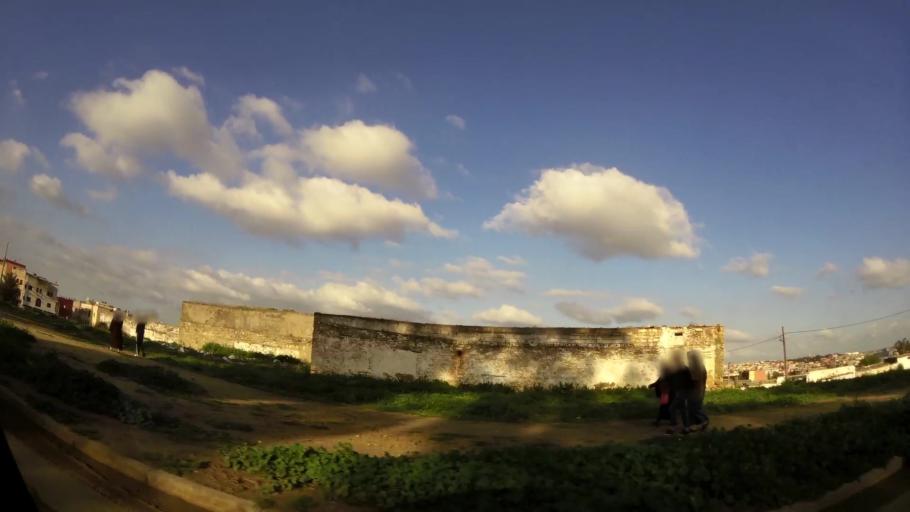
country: MA
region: Chaouia-Ouardigha
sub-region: Settat Province
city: Settat
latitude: 33.0013
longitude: -7.6272
